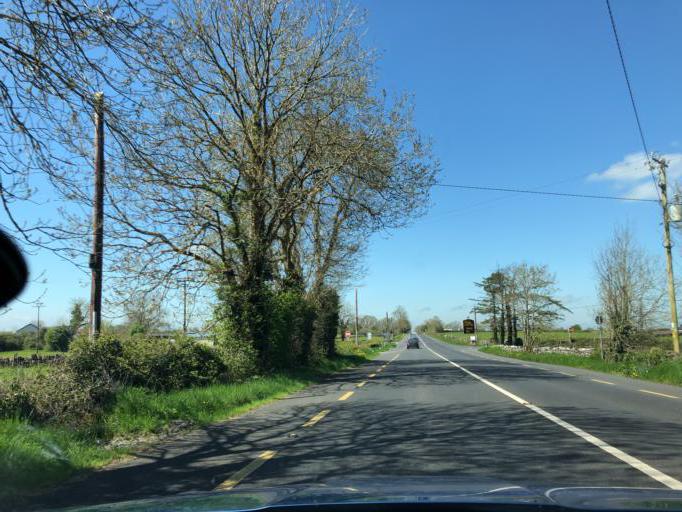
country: IE
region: Connaught
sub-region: County Galway
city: Loughrea
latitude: 53.2089
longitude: -8.6366
